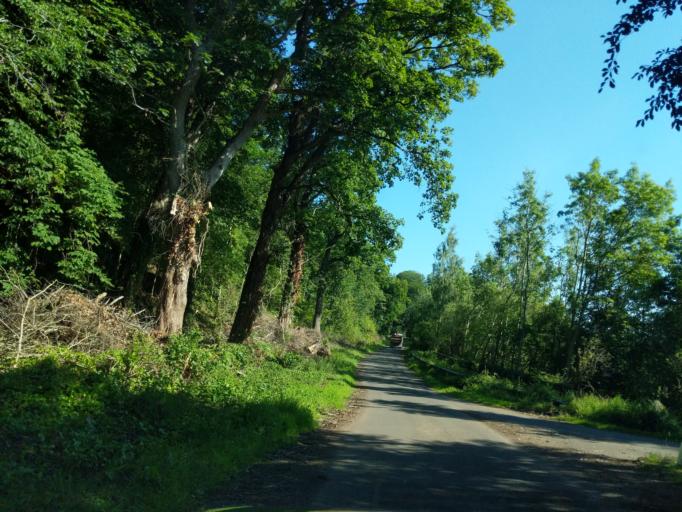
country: GB
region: Scotland
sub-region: Fife
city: Pathhead
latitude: 55.8749
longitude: -2.9720
